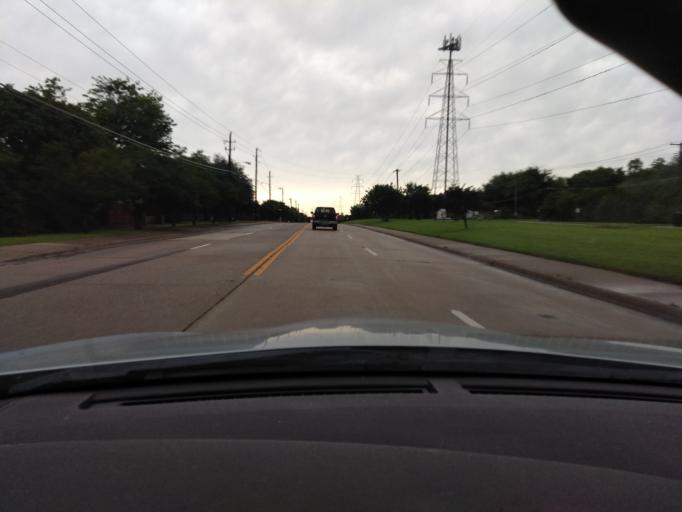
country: US
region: Texas
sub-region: Dallas County
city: Addison
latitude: 32.9670
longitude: -96.7785
